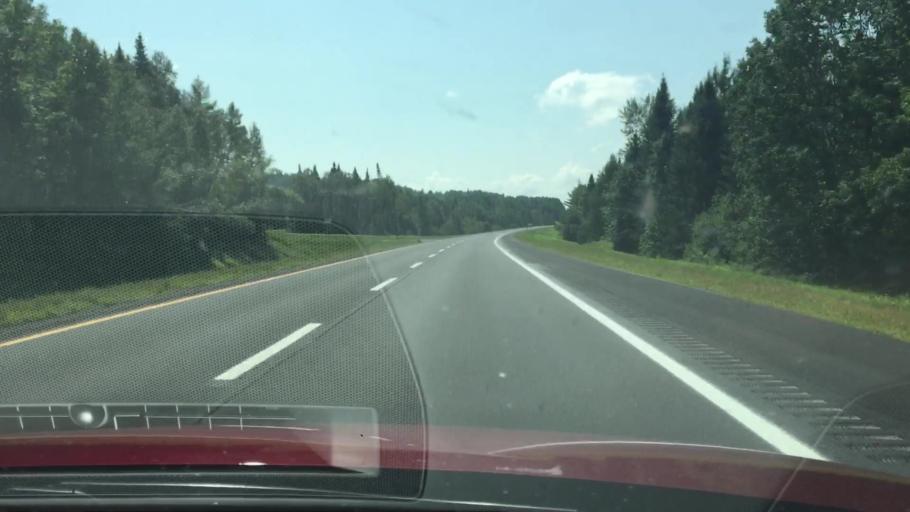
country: US
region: Maine
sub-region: Penobscot County
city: Patten
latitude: 45.9211
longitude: -68.3692
